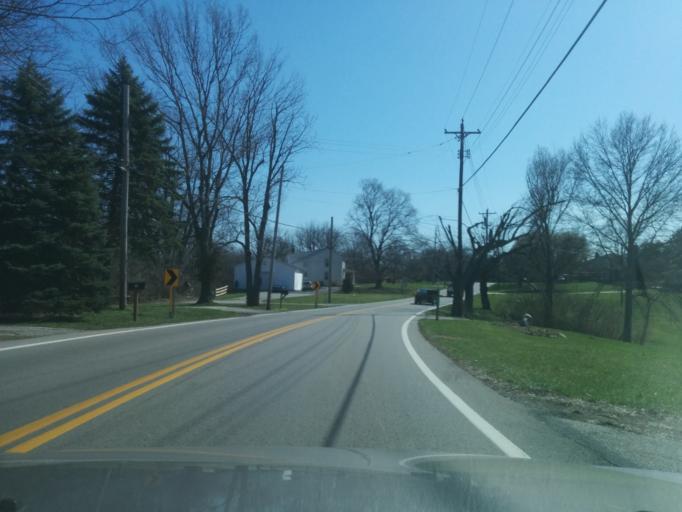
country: US
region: Ohio
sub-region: Hamilton County
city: Monfort Heights
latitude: 39.1940
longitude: -84.6223
